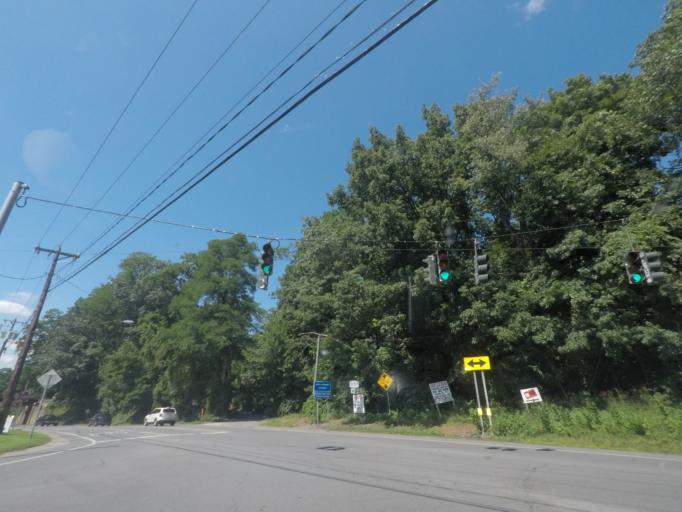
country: US
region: New York
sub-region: Schenectady County
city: Rotterdam
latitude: 42.8052
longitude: -73.9906
